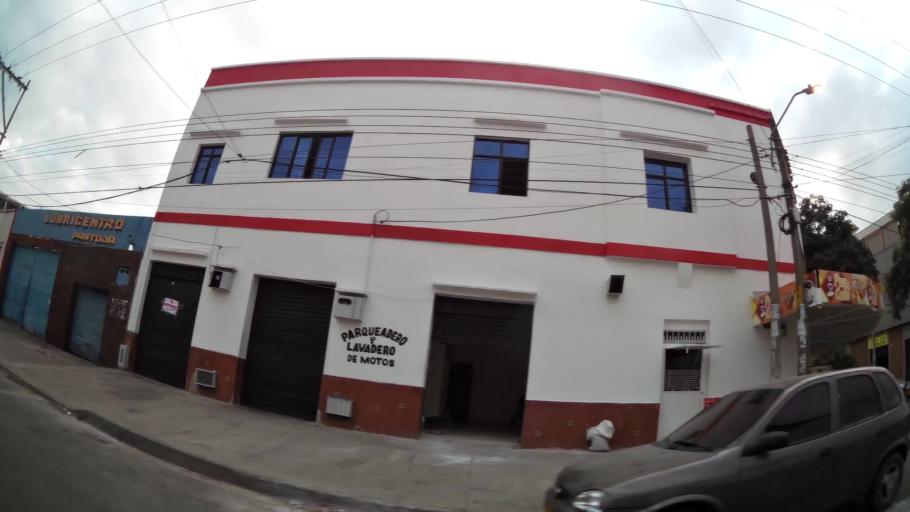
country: CO
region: Valle del Cauca
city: Cali
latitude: 3.4596
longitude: -76.5255
